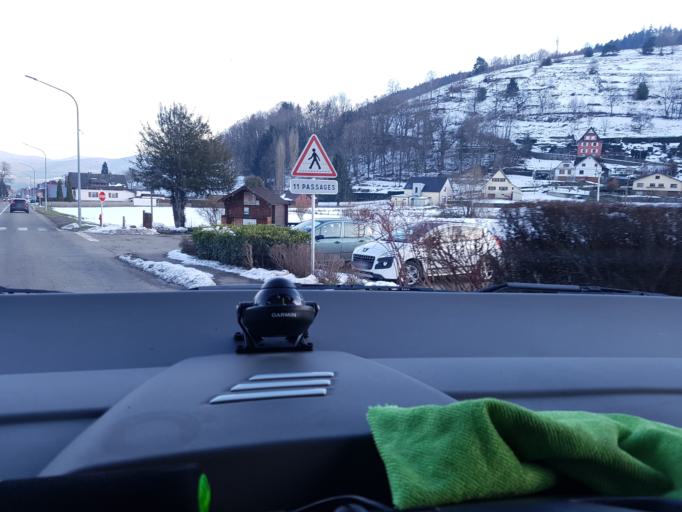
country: FR
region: Alsace
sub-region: Departement du Haut-Rhin
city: Soultzeren
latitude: 48.0537
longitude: 7.1005
